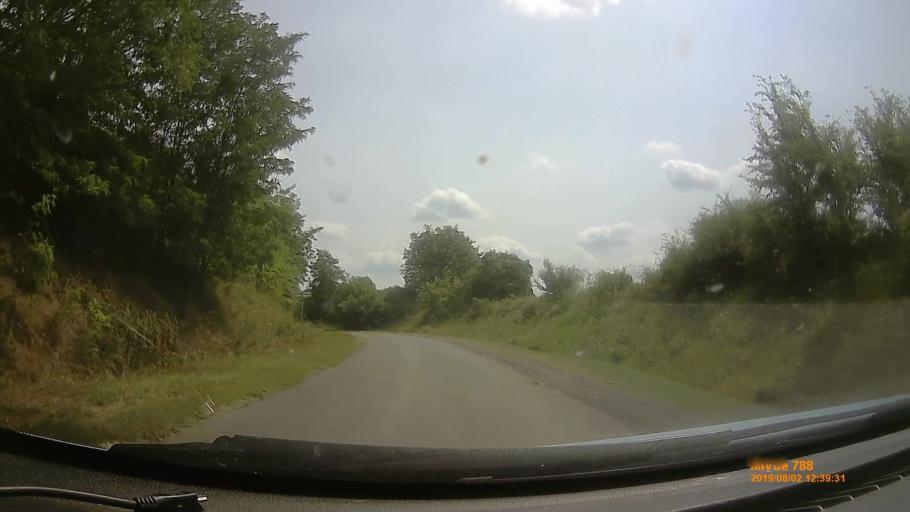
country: HU
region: Baranya
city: Buekkoesd
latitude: 46.0891
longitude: 17.9604
